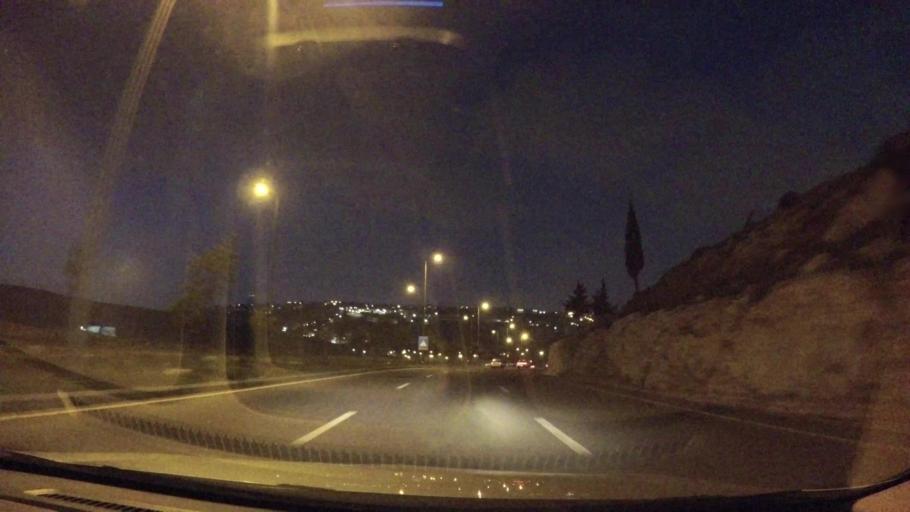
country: JO
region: Amman
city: Al Bunayyat ash Shamaliyah
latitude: 31.9247
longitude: 35.8783
